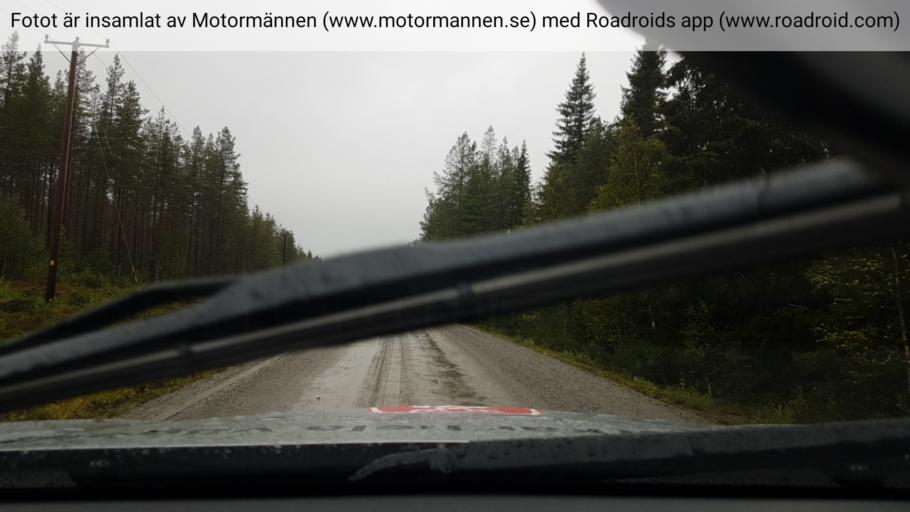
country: SE
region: Vaesterbotten
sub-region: Asele Kommun
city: Insjon
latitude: 64.0878
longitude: 17.8523
